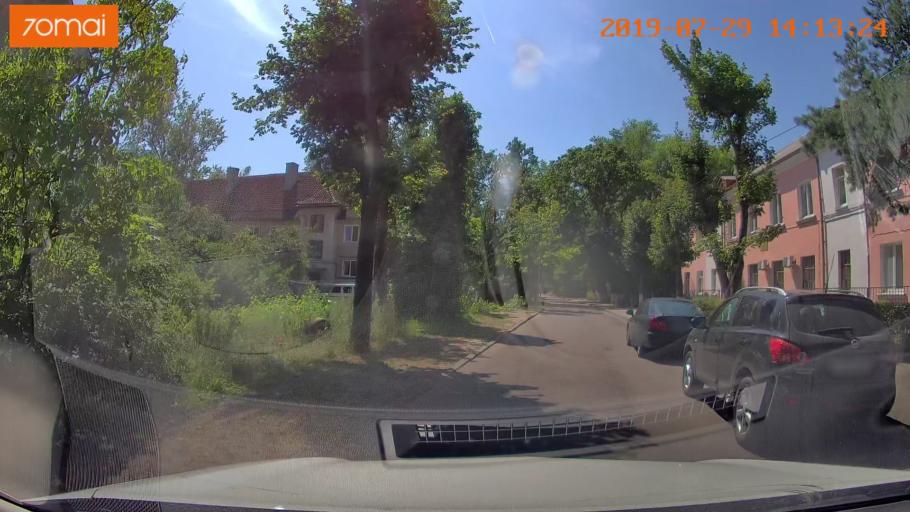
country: RU
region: Kaliningrad
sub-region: Gorod Kaliningrad
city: Baltiysk
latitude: 54.6507
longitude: 19.9029
